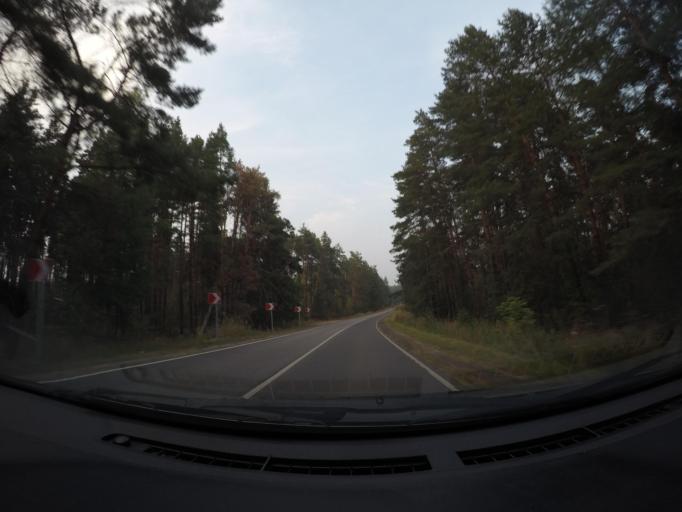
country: RU
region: Moskovskaya
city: Imeni Tsyurupy
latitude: 55.4947
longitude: 38.6834
